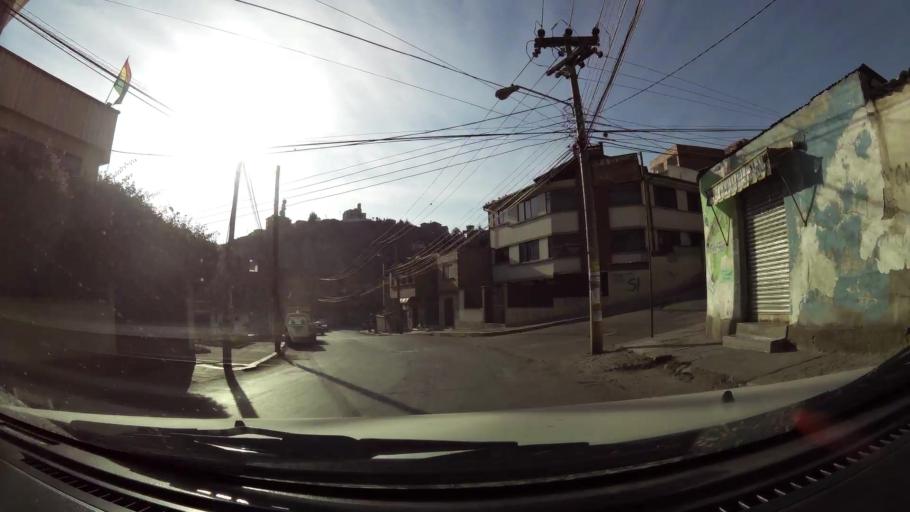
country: BO
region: La Paz
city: La Paz
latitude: -16.5263
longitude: -68.0990
